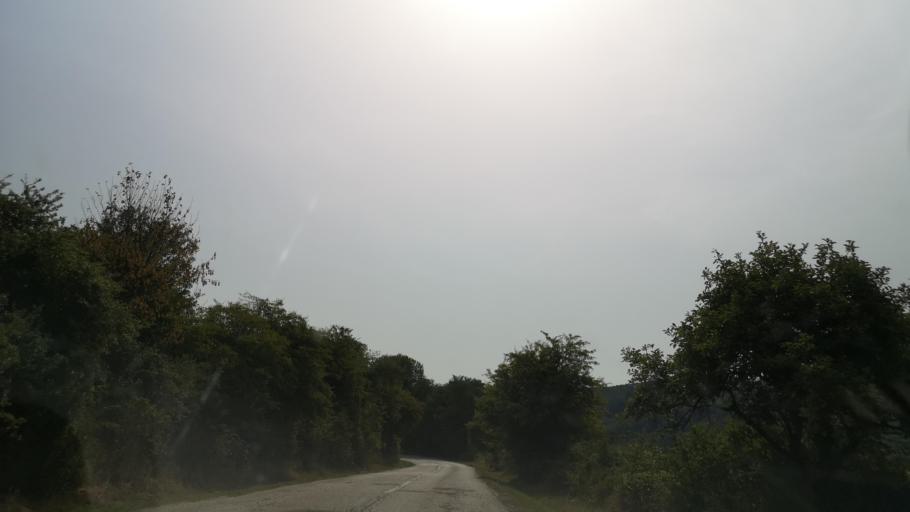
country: SK
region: Banskobystricky
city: Revuca
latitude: 48.5995
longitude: 20.1369
